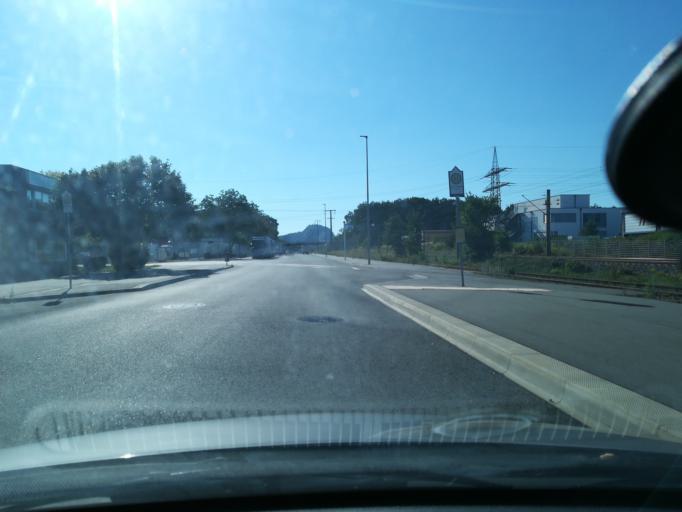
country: DE
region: Baden-Wuerttemberg
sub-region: Freiburg Region
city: Singen
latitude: 47.7584
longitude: 8.8839
